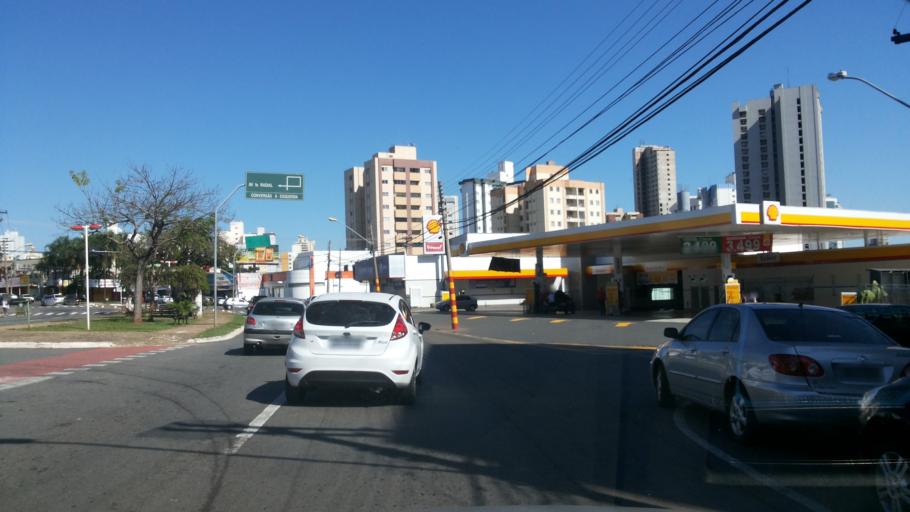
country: BR
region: Goias
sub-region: Goiania
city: Goiania
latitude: -16.7118
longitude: -49.2526
